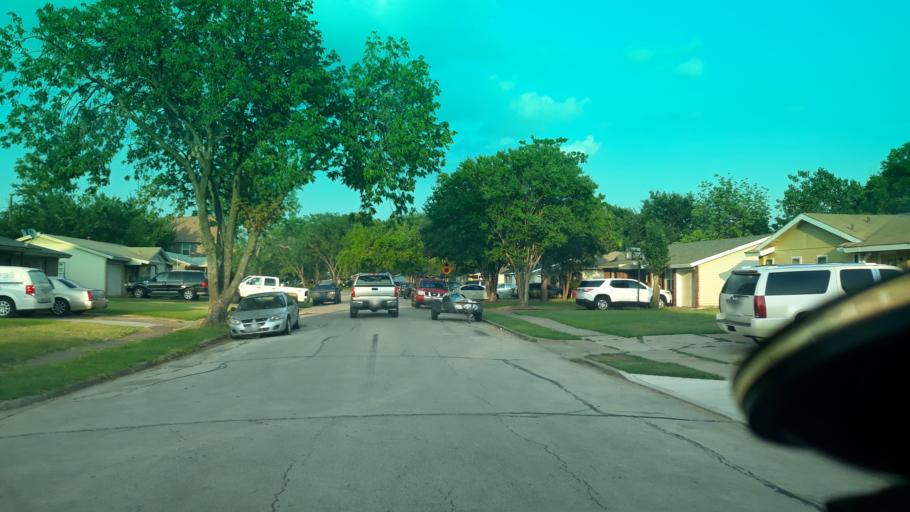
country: US
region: Texas
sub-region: Dallas County
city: Irving
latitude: 32.8429
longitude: -96.9798
